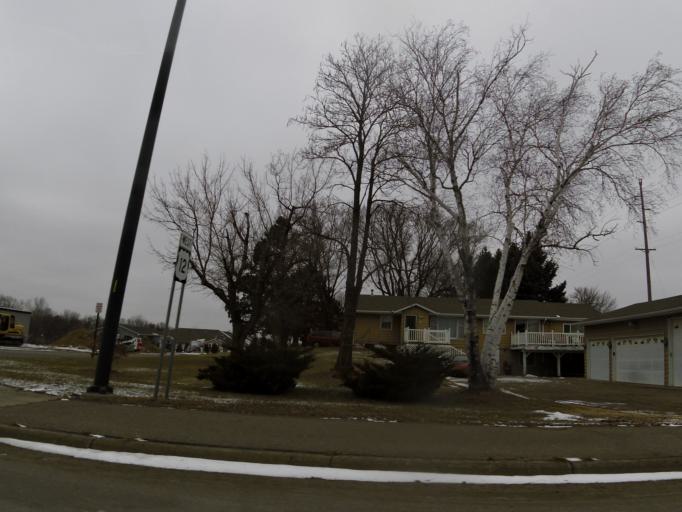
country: US
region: Minnesota
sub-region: Wright County
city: Delano
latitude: 45.0356
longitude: -93.7771
